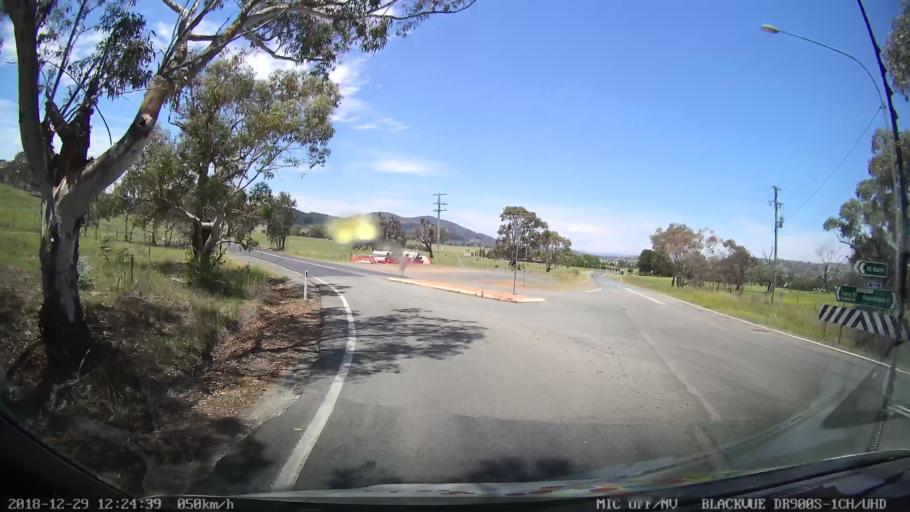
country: AU
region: Australian Capital Territory
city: Macarthur
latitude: -35.4490
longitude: 149.2097
